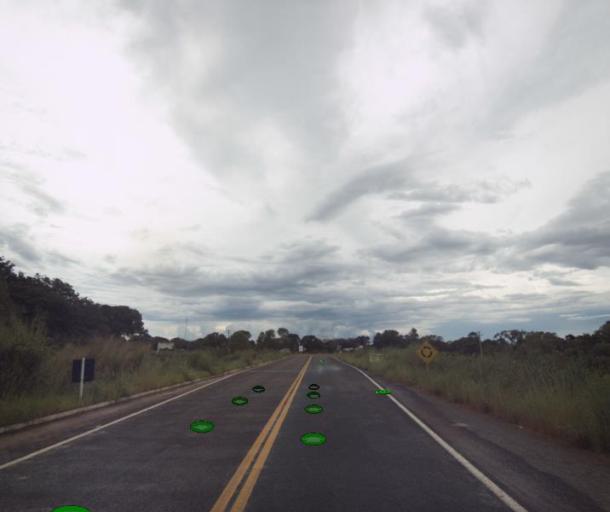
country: BR
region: Goias
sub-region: Sao Miguel Do Araguaia
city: Sao Miguel do Araguaia
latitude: -13.2194
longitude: -50.5732
